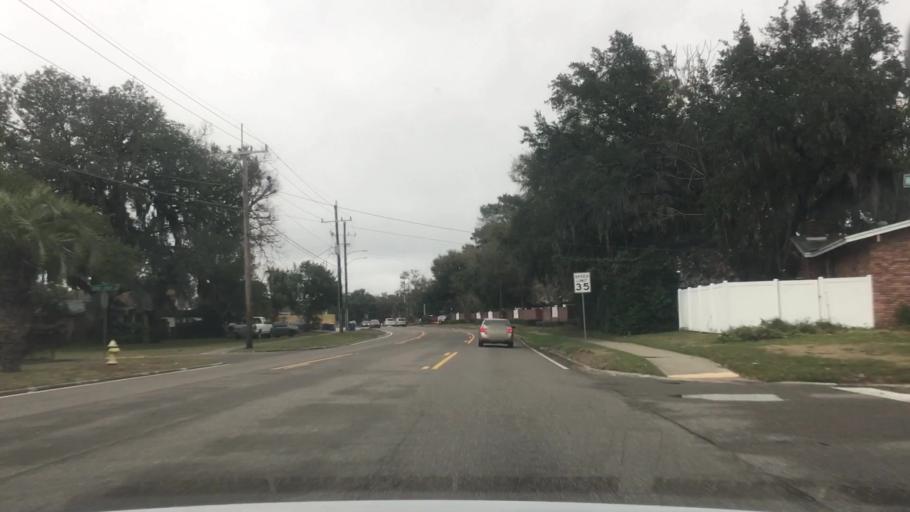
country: US
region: Florida
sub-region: Duval County
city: Jacksonville
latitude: 30.3587
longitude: -81.5775
